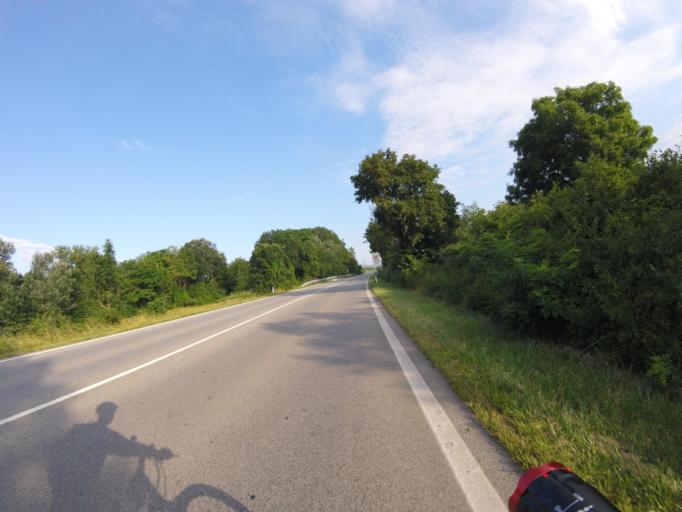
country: AT
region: Lower Austria
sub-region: Politischer Bezirk Baden
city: Ebreichsdorf
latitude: 47.9880
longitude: 16.3865
